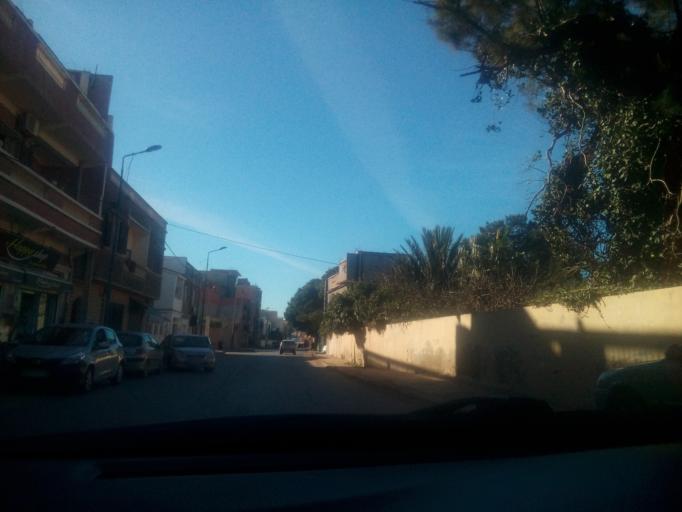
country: DZ
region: Oran
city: Bir el Djir
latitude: 35.7520
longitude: -0.5649
